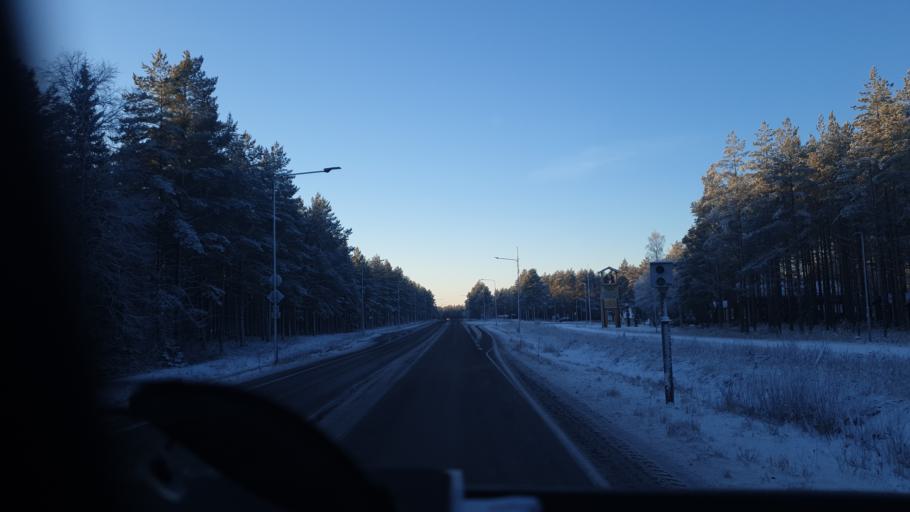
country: FI
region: Northern Ostrobothnia
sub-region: Ylivieska
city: Kalajoki
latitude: 64.2413
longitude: 23.8472
